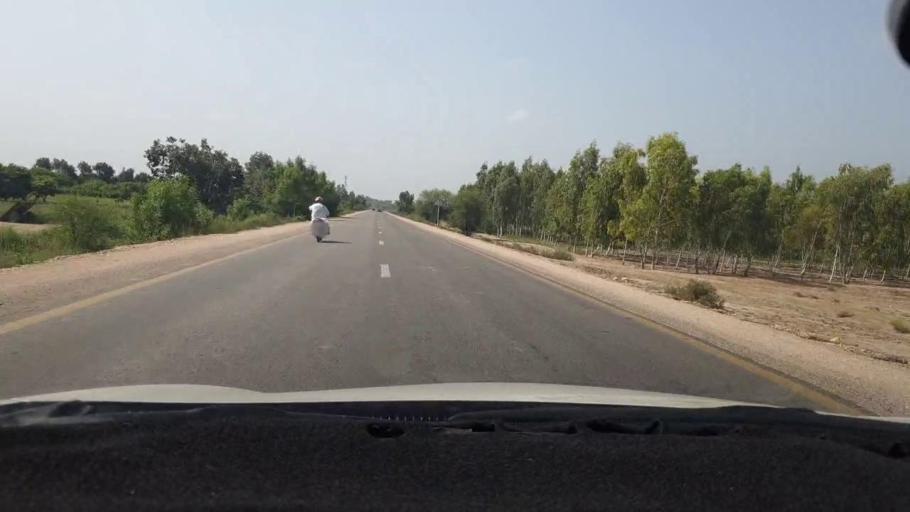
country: PK
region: Sindh
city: Mirpur Khas
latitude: 25.6714
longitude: 69.1058
